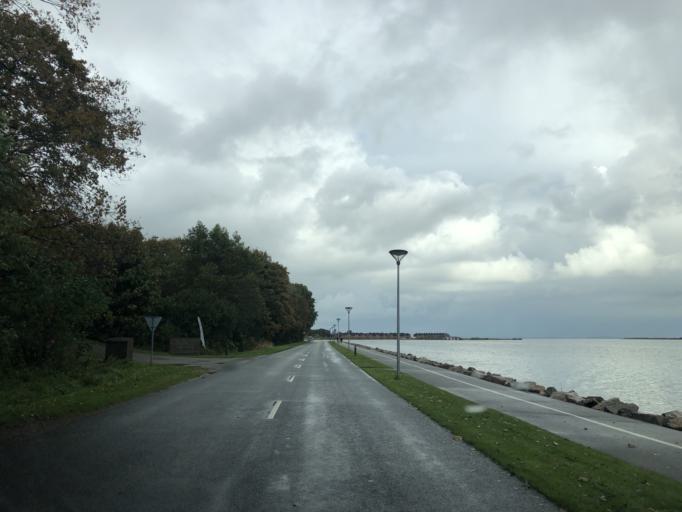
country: DK
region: Central Jutland
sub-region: Lemvig Kommune
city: Lemvig
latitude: 56.5573
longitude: 8.2955
